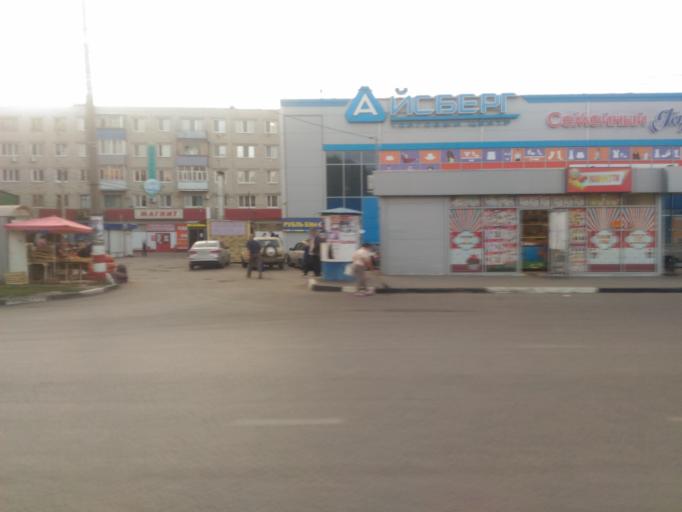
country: RU
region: Ulyanovsk
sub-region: Ulyanovskiy Rayon
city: Ulyanovsk
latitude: 54.2750
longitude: 48.2894
